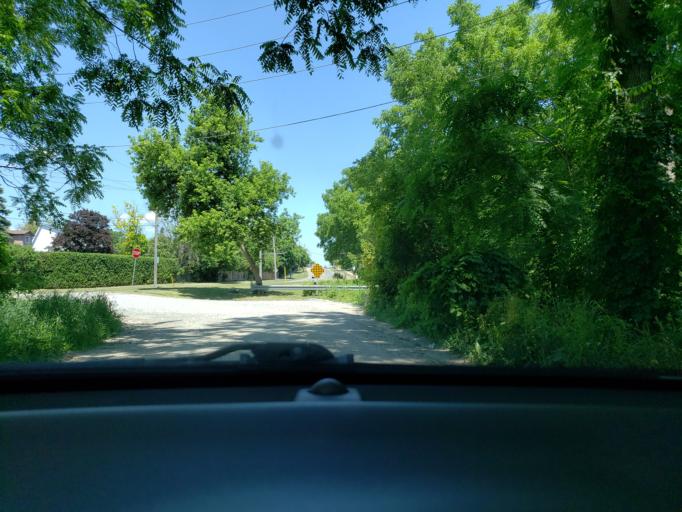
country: CA
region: Ontario
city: Newmarket
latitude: 44.0705
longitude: -79.4584
